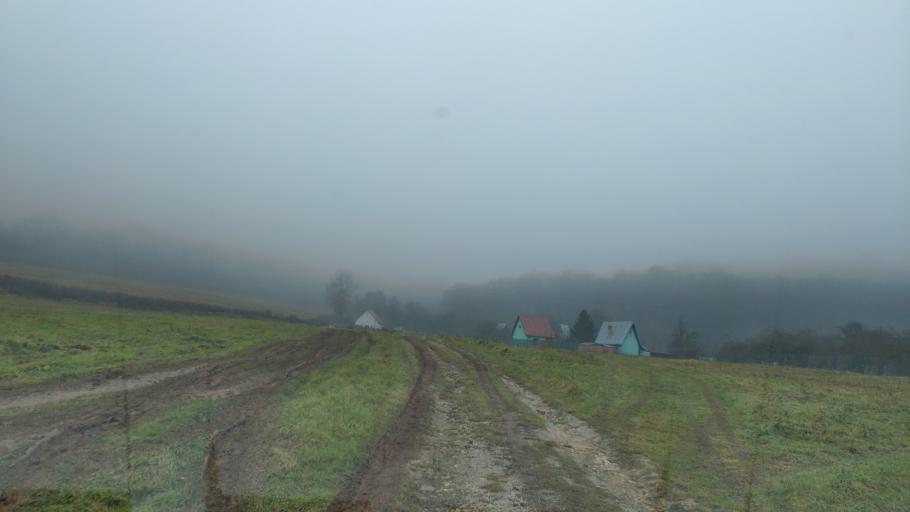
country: SK
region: Banskobystricky
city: Revuca
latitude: 48.6508
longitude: 20.2576
